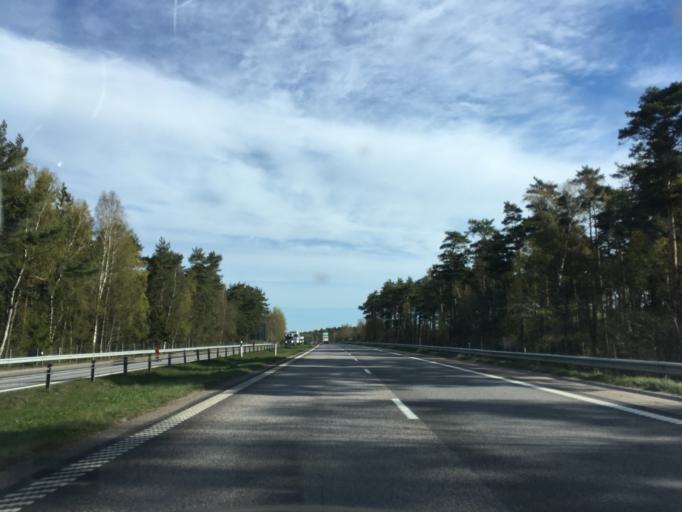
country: SE
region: Halland
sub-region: Laholms Kommun
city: Mellbystrand
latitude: 56.5127
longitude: 12.9636
